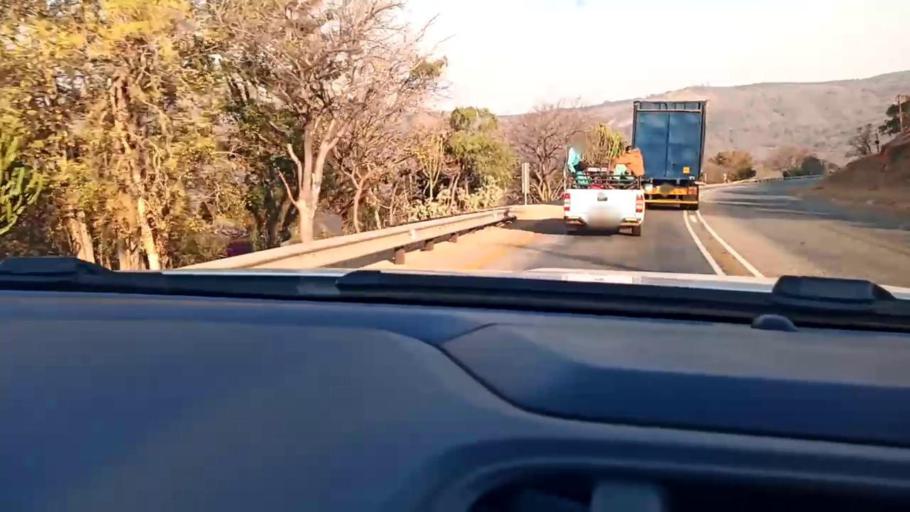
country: ZA
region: Limpopo
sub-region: Mopani District Municipality
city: Ga-Kgapane
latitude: -23.6478
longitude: 30.1709
